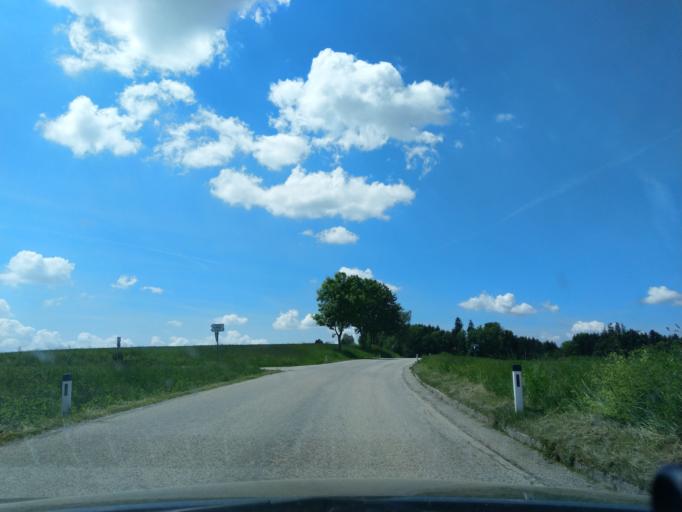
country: AT
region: Upper Austria
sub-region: Politischer Bezirk Ried im Innkreis
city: Ried im Innkreis
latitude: 48.1996
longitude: 13.5926
